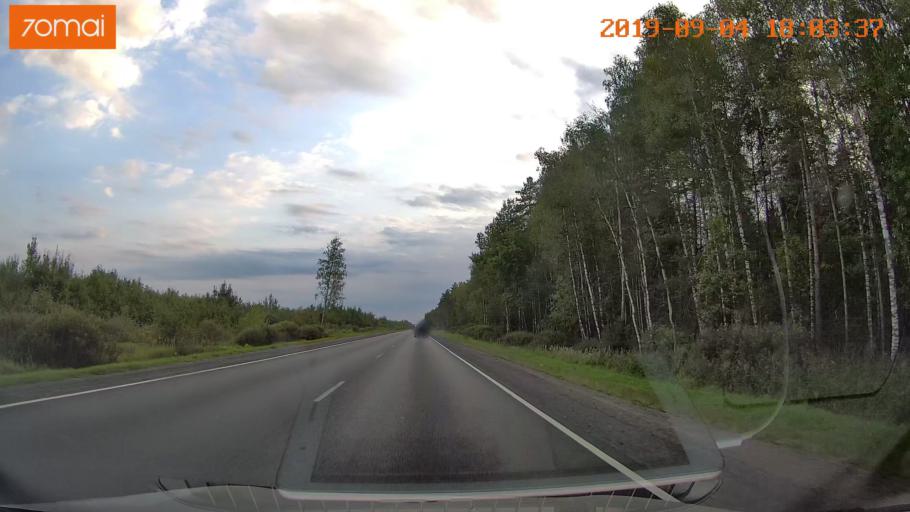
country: RU
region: Moskovskaya
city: Il'inskiy Pogost
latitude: 55.4613
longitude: 38.8497
